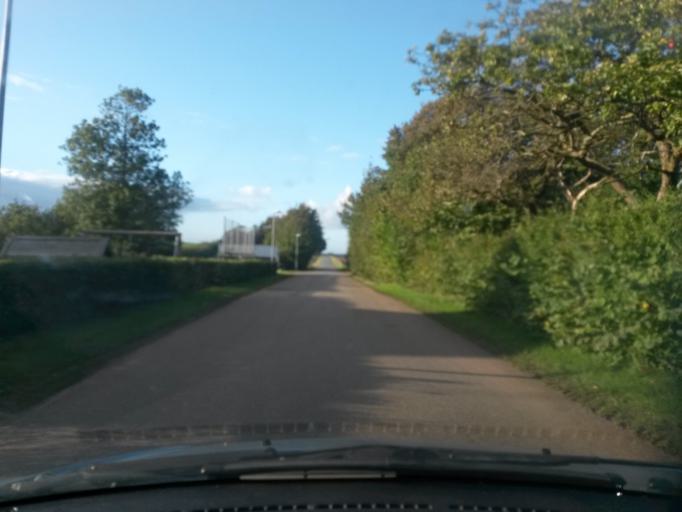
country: DK
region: Central Jutland
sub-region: Viborg Kommune
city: Viborg
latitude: 56.3769
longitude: 9.3971
